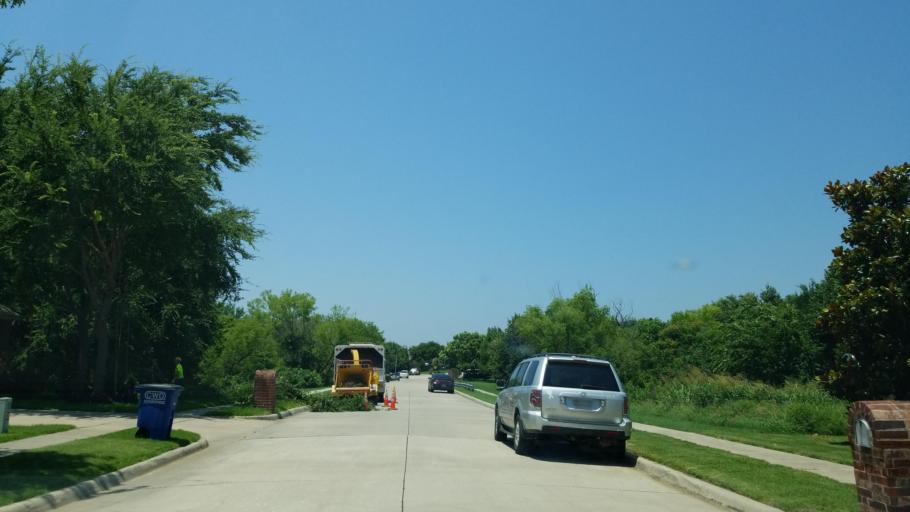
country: US
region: Texas
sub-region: Denton County
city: Hickory Creek
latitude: 33.1350
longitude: -97.0393
